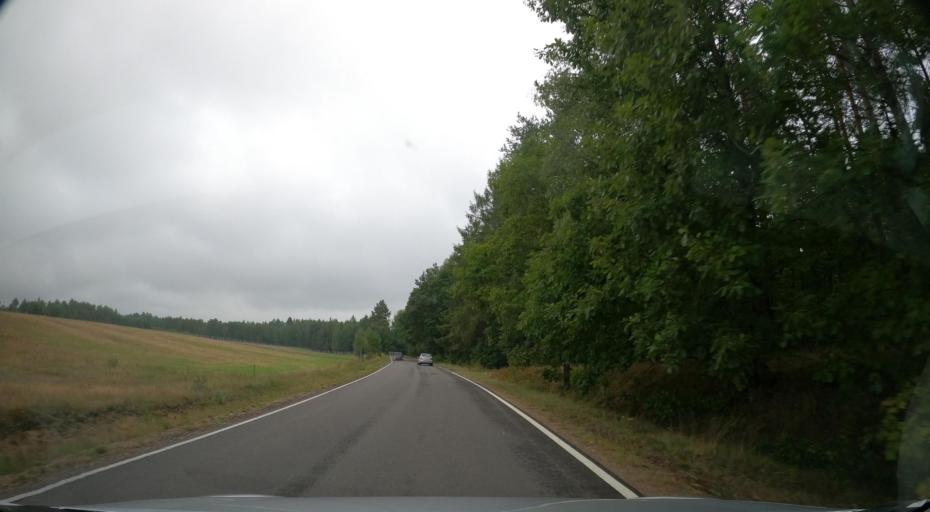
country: PL
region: Pomeranian Voivodeship
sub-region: Powiat wejherowski
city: Leczyce
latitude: 54.4939
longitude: 17.8416
